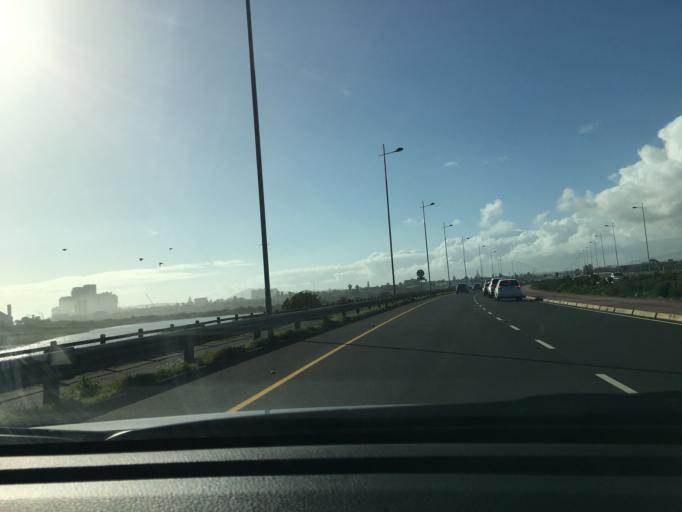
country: ZA
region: Western Cape
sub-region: City of Cape Town
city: Sunset Beach
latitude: -33.8329
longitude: 18.4841
